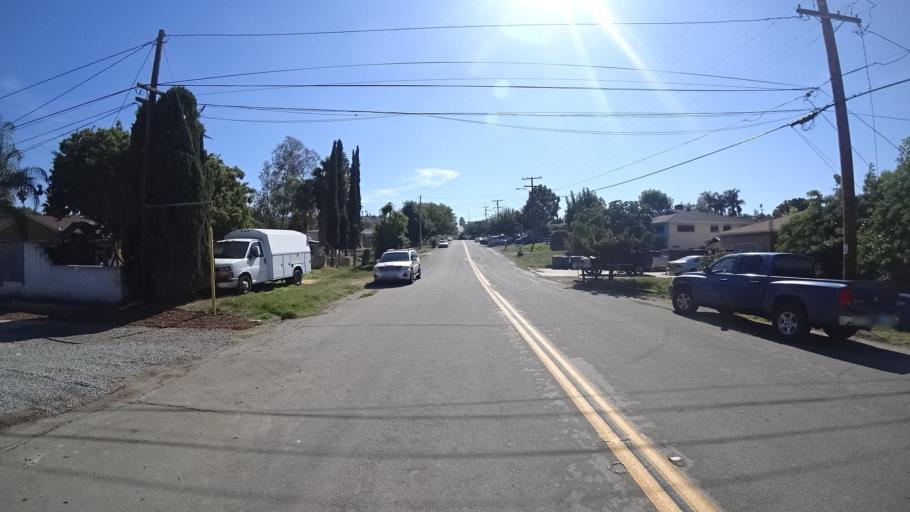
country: US
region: California
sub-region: San Diego County
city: Spring Valley
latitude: 32.7463
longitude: -116.9790
